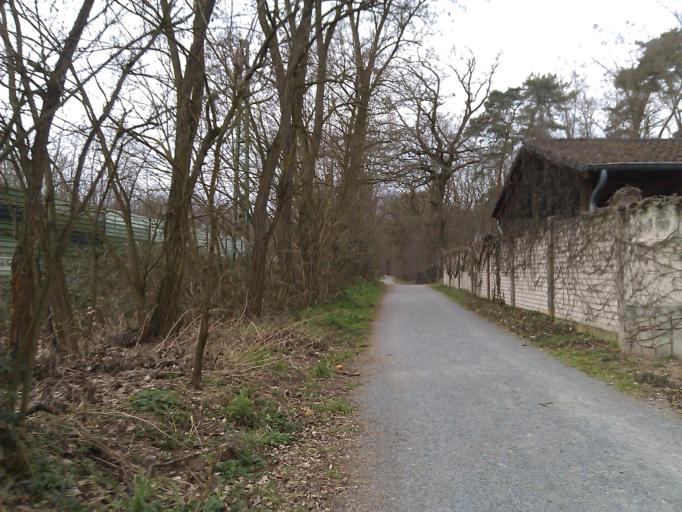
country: DE
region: Hesse
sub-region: Regierungsbezirk Darmstadt
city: Nauheim
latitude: 49.9482
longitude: 8.4393
